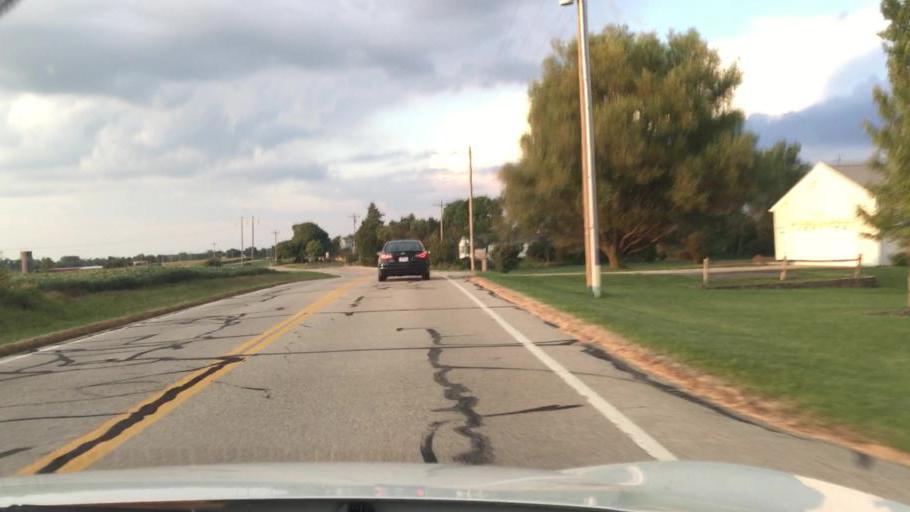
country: US
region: Ohio
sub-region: Champaign County
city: Mechanicsburg
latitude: 40.0295
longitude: -83.5751
